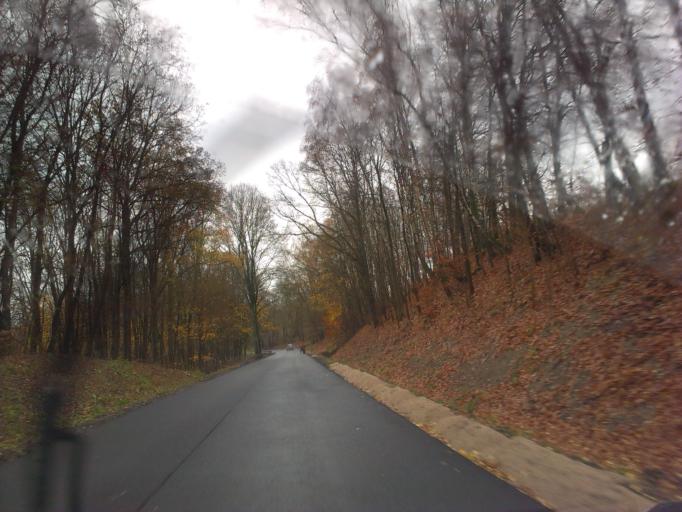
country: PL
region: West Pomeranian Voivodeship
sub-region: Powiat szczecinecki
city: Borne Sulinowo
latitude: 53.6237
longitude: 16.5147
